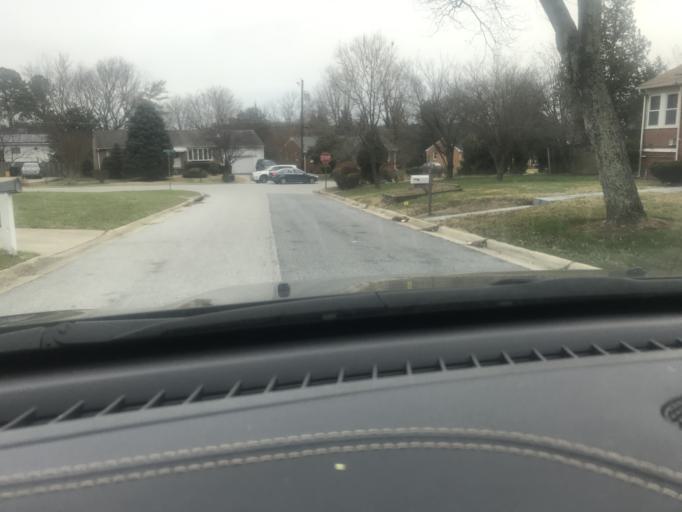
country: US
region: Maryland
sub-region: Prince George's County
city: Oxon Hill
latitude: 38.7981
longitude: -76.9717
